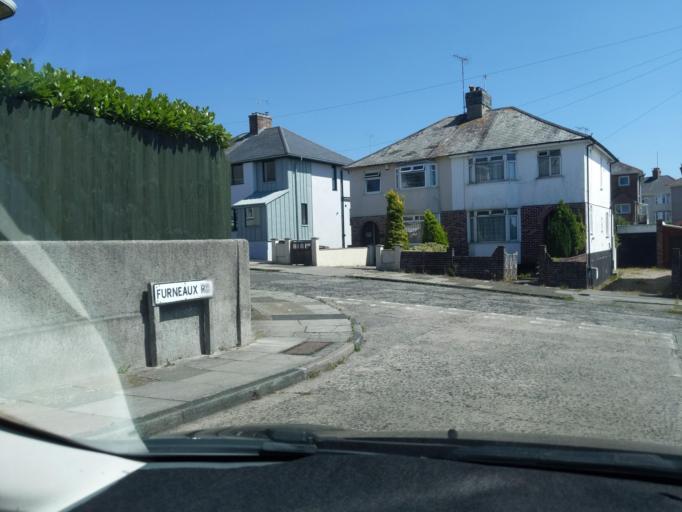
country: GB
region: England
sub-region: Plymouth
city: Plymouth
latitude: 50.3906
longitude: -4.1561
